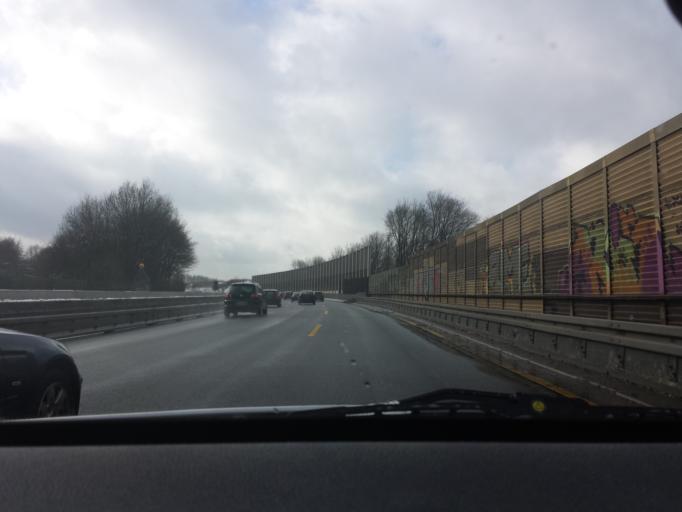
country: DE
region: North Rhine-Westphalia
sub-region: Regierungsbezirk Dusseldorf
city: Solingen
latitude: 51.2192
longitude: 7.0605
